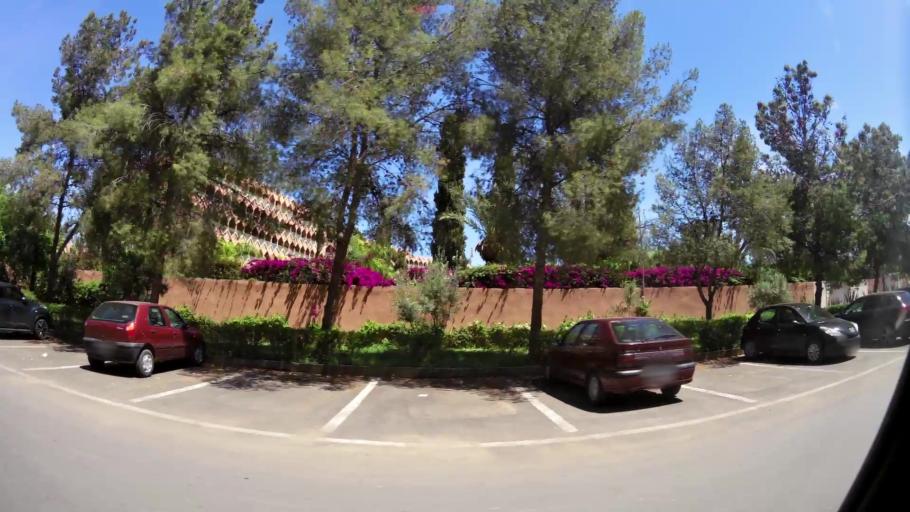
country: MA
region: Marrakech-Tensift-Al Haouz
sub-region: Marrakech
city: Marrakesh
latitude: 31.6222
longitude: -8.0135
